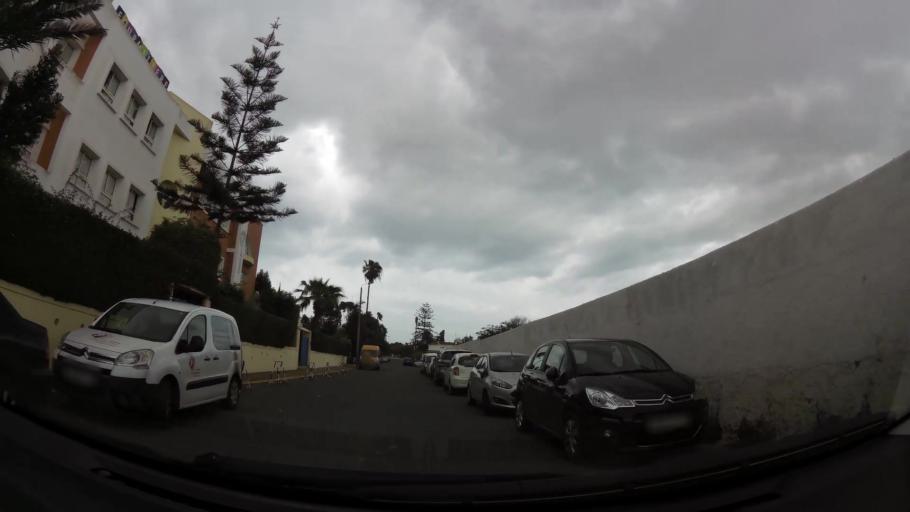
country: MA
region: Grand Casablanca
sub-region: Casablanca
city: Casablanca
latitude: 33.5809
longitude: -7.6653
